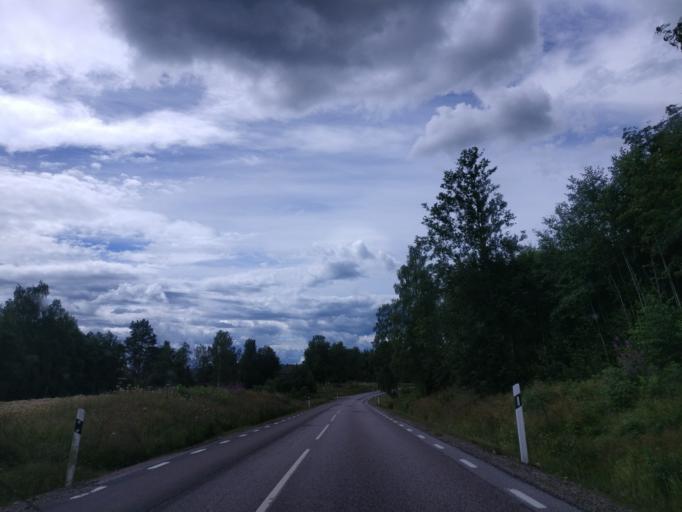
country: SE
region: Vaermland
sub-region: Hagfors Kommun
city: Ekshaerad
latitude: 60.1540
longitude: 13.4416
